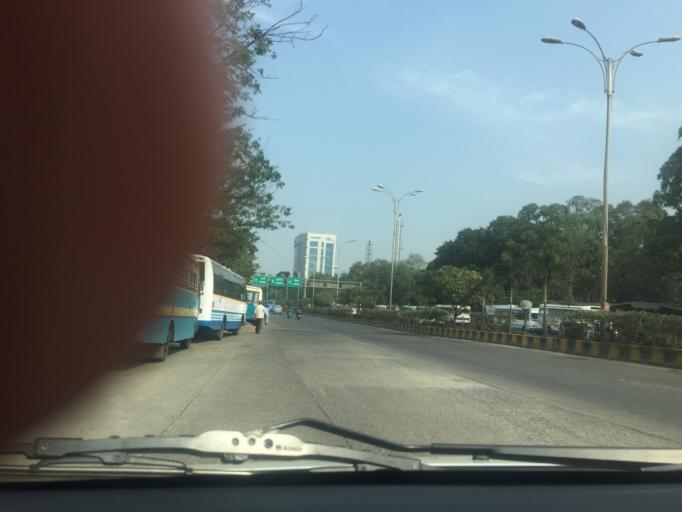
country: IN
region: Maharashtra
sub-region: Thane
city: Airoli
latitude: 19.1502
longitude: 73.0005
